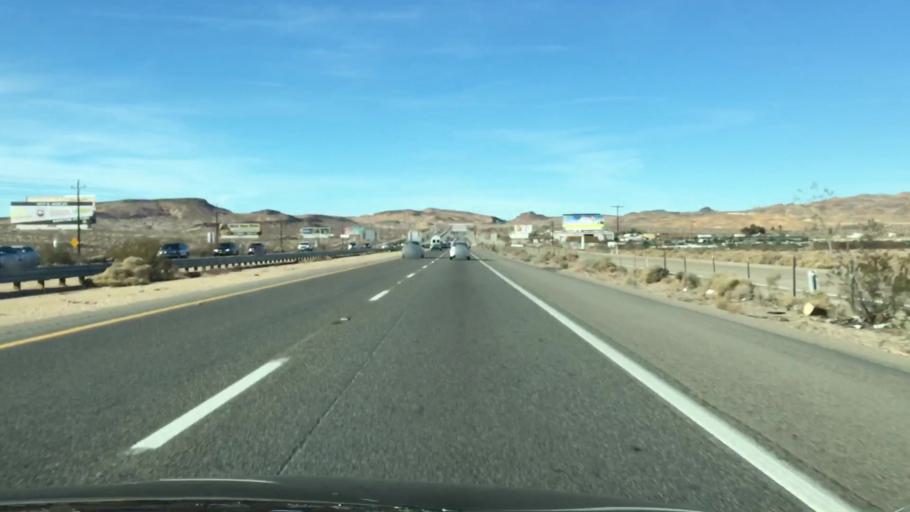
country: US
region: California
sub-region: San Bernardino County
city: Barstow
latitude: 34.9013
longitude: -116.9002
